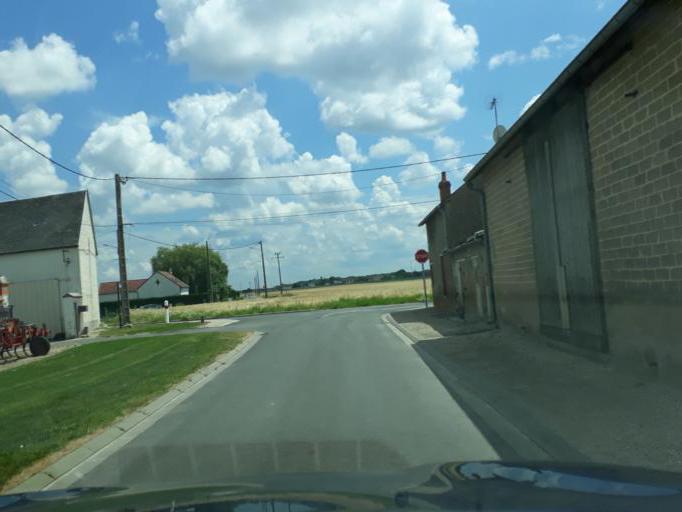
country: FR
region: Centre
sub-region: Departement du Loiret
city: Chevilly
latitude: 48.0400
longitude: 1.9123
